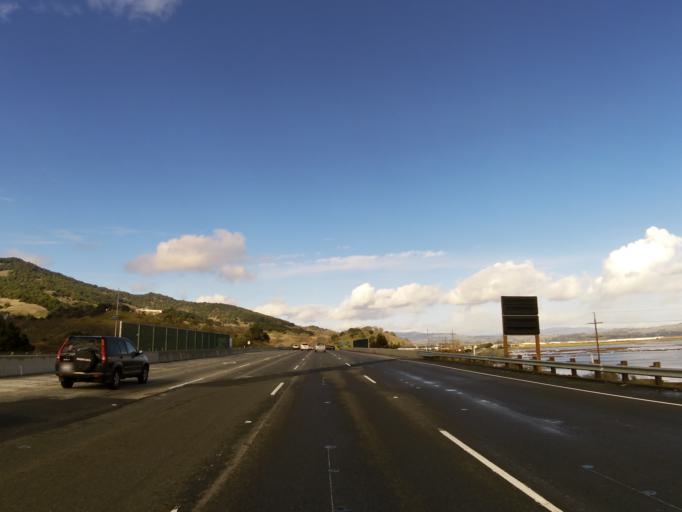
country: US
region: California
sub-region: Marin County
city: Novato
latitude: 38.1213
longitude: -122.5655
